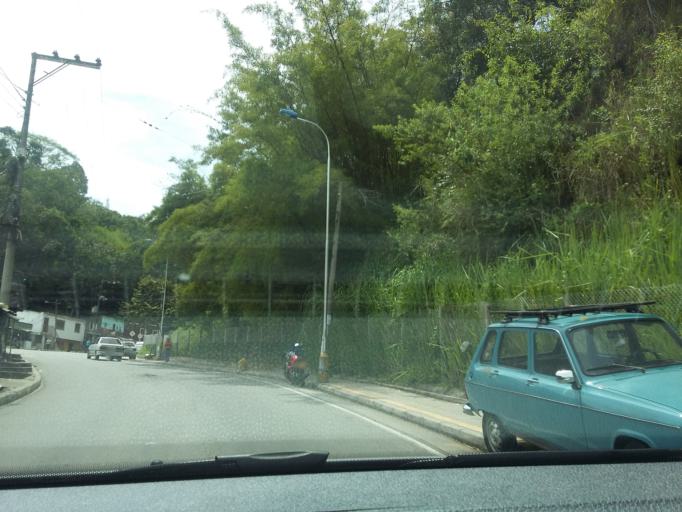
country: CO
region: Santander
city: Bucaramanga
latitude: 7.1340
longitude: -73.1066
